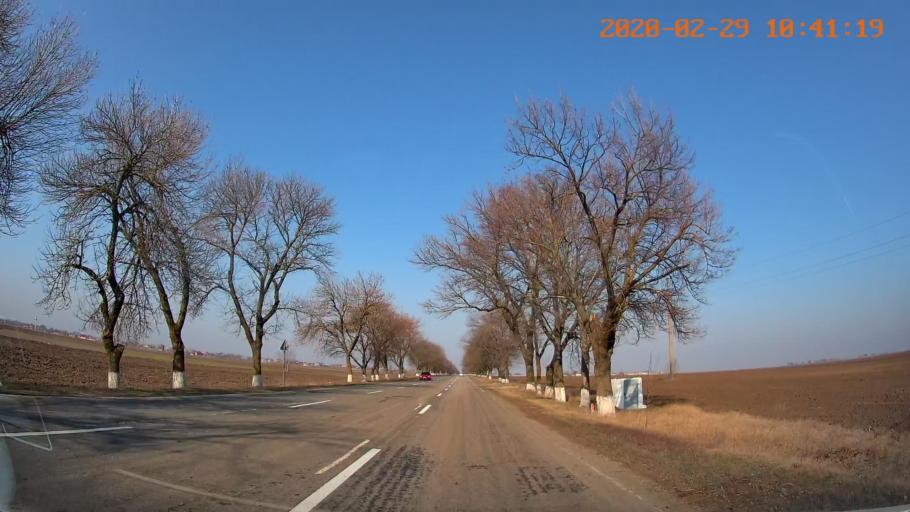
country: MD
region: Telenesti
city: Grigoriopol
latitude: 47.0413
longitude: 29.4269
